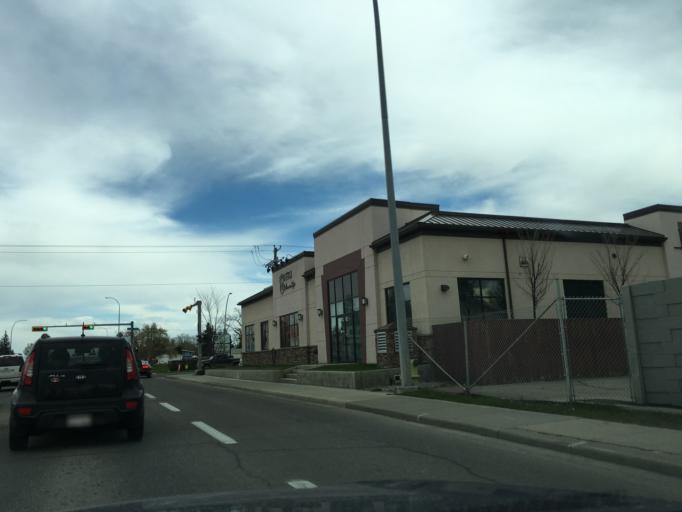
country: CA
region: Alberta
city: Calgary
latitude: 50.9640
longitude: -114.0494
